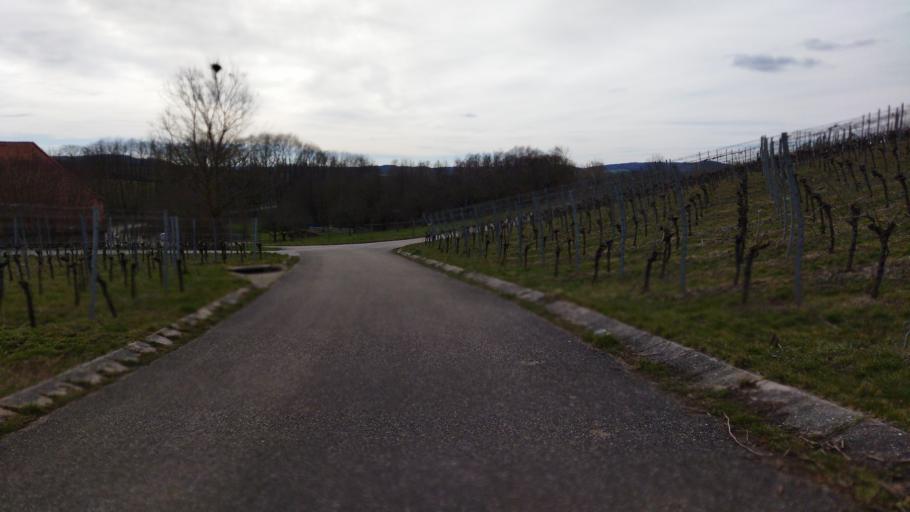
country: DE
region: Baden-Wuerttemberg
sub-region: Regierungsbezirk Stuttgart
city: Bretzfeld
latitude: 49.1741
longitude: 9.4571
